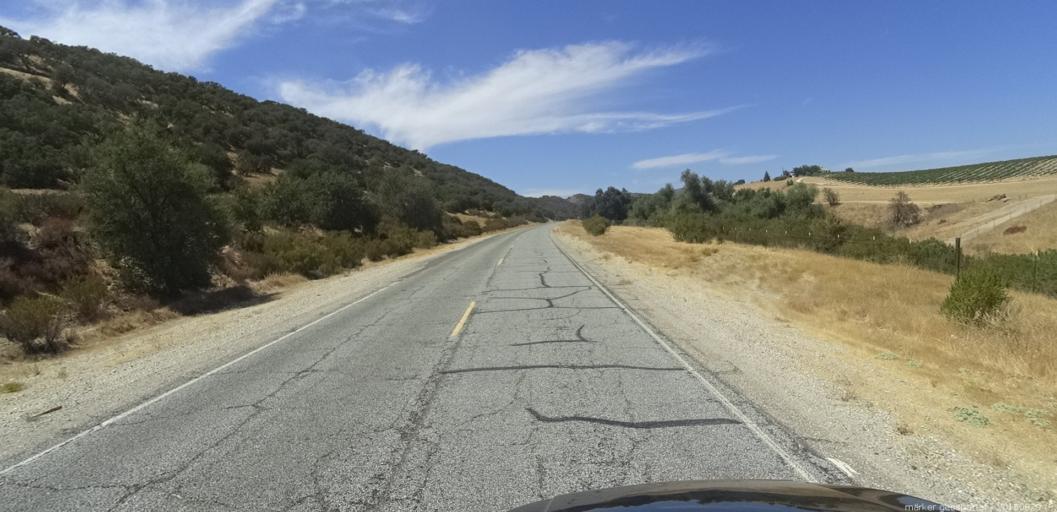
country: US
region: California
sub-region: San Luis Obispo County
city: Lake Nacimiento
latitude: 35.8885
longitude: -120.9244
